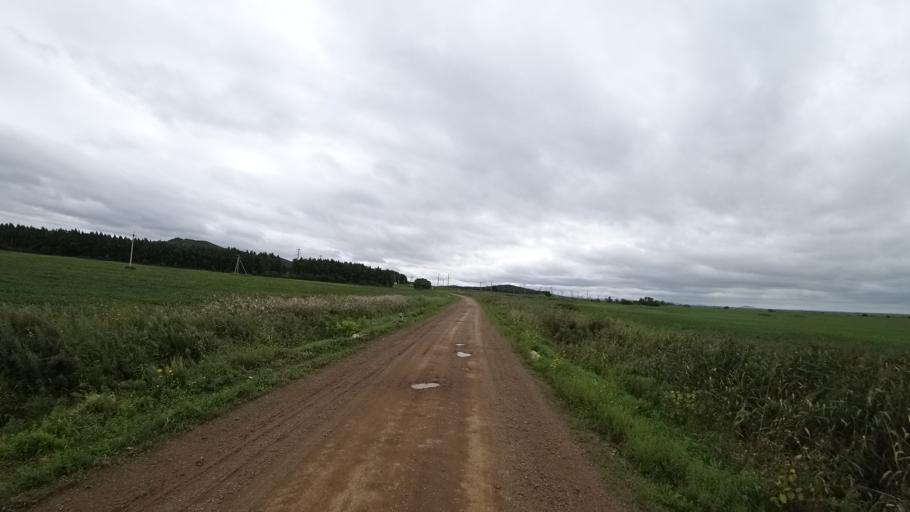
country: RU
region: Primorskiy
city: Chernigovka
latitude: 44.4824
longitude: 132.5744
